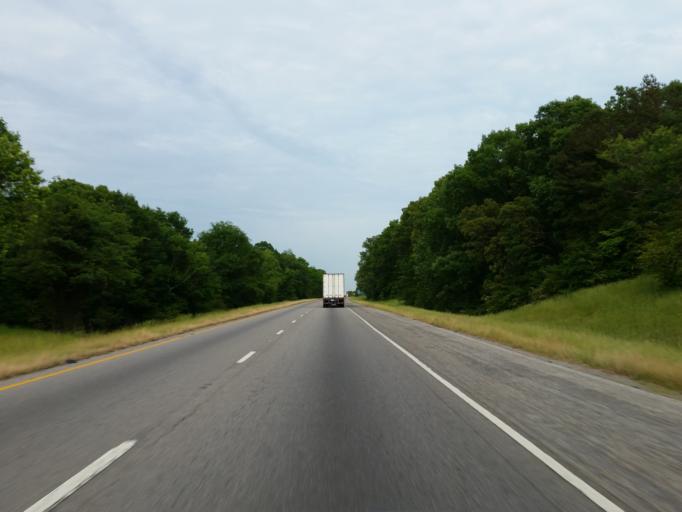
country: US
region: Alabama
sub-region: Talladega County
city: Lincoln
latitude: 33.5901
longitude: -86.1161
